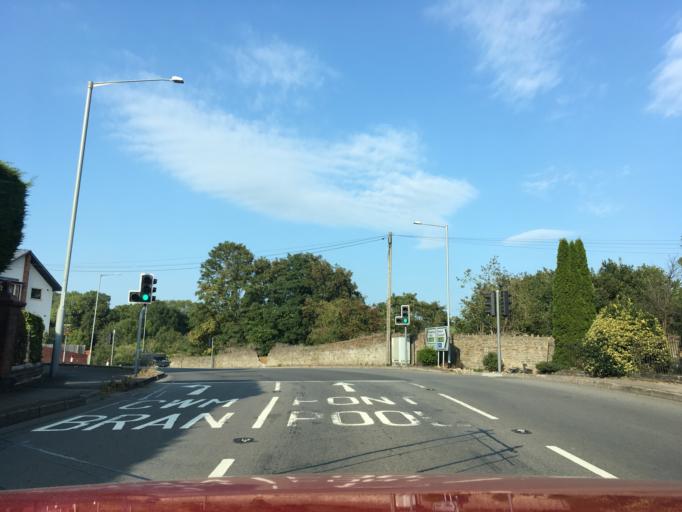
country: GB
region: Wales
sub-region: Torfaen County Borough
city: Ponthir
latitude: 51.6337
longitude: -3.0025
